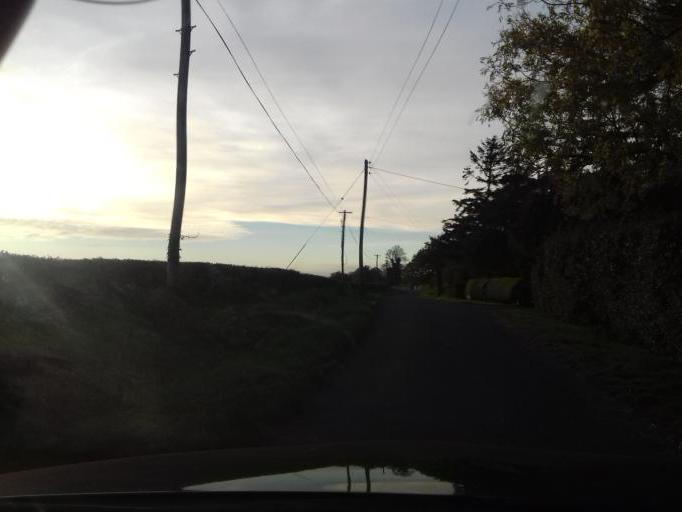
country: IE
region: Leinster
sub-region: An Mhi
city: Dunboyne
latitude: 53.3898
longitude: -6.4730
